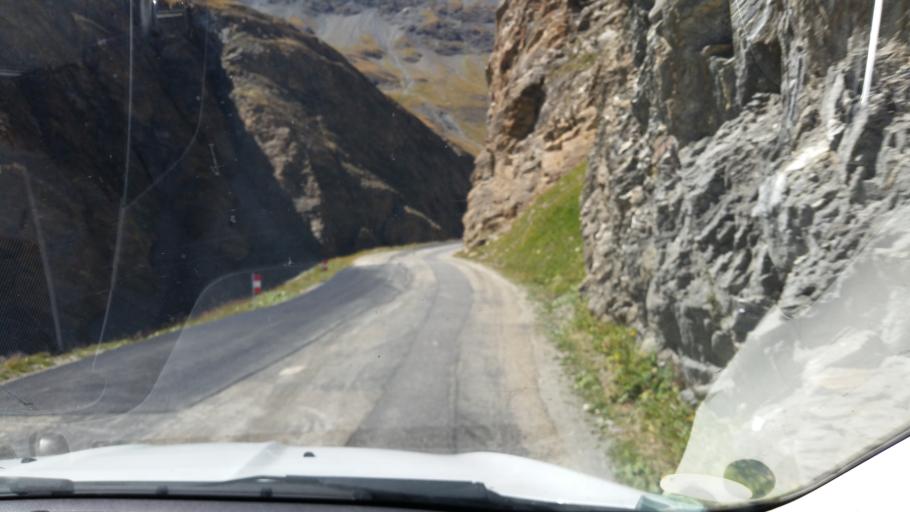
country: FR
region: Rhone-Alpes
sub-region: Departement de la Savoie
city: Val-d'Isere
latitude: 45.4029
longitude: 7.0338
